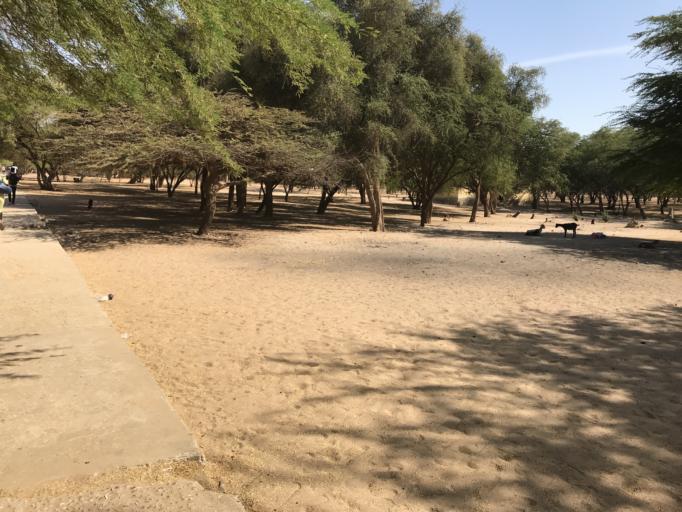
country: SN
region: Saint-Louis
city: Saint-Louis
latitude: 16.0648
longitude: -16.4228
